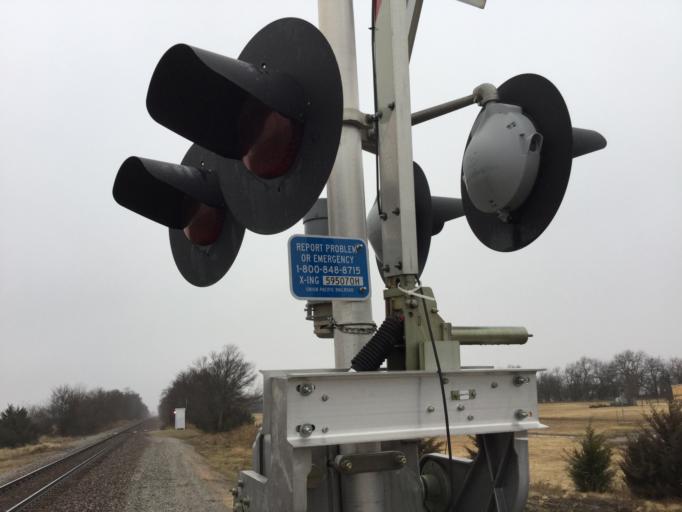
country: US
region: Kansas
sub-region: Sedgwick County
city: Haysville
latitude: 37.5354
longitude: -97.3592
